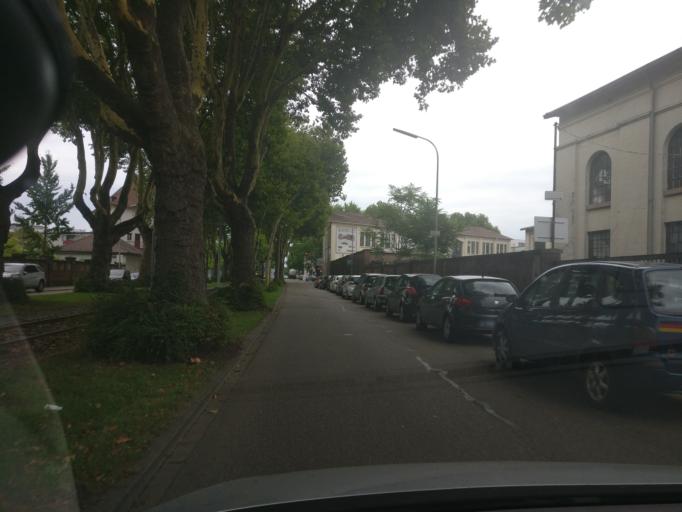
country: DE
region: Baden-Wuerttemberg
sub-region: Karlsruhe Region
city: Karlsruhe
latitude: 49.0009
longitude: 8.4663
